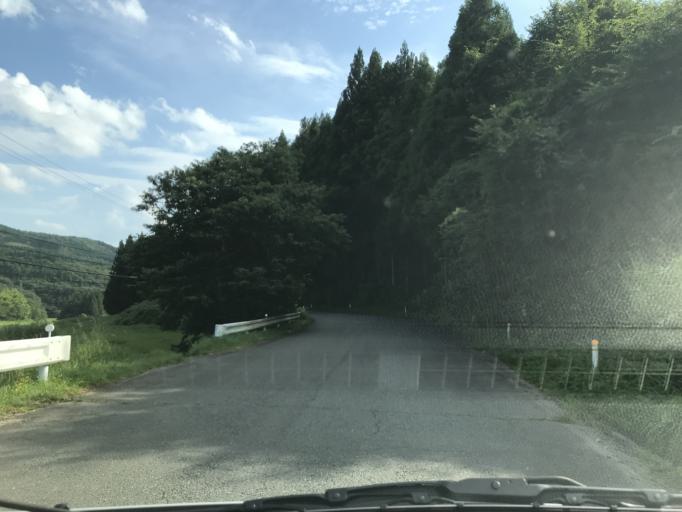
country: JP
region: Iwate
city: Ofunato
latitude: 38.9611
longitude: 141.4716
